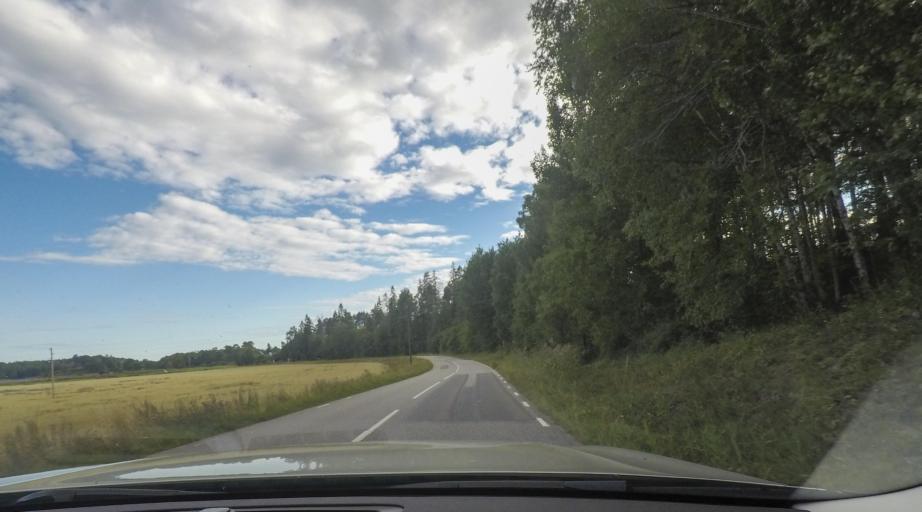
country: SE
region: Soedermanland
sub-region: Trosa Kommun
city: Trosa
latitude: 58.9718
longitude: 17.6942
